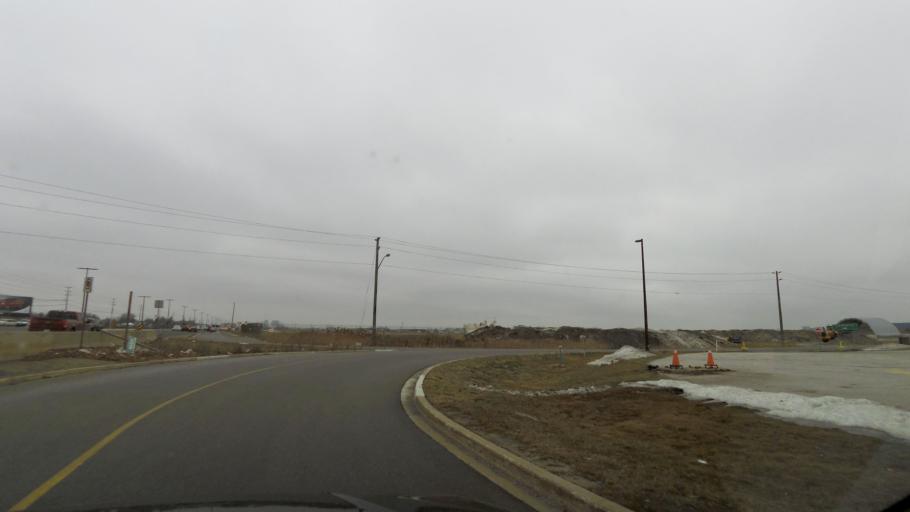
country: CA
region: Ontario
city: Etobicoke
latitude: 43.6950
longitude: -79.6519
